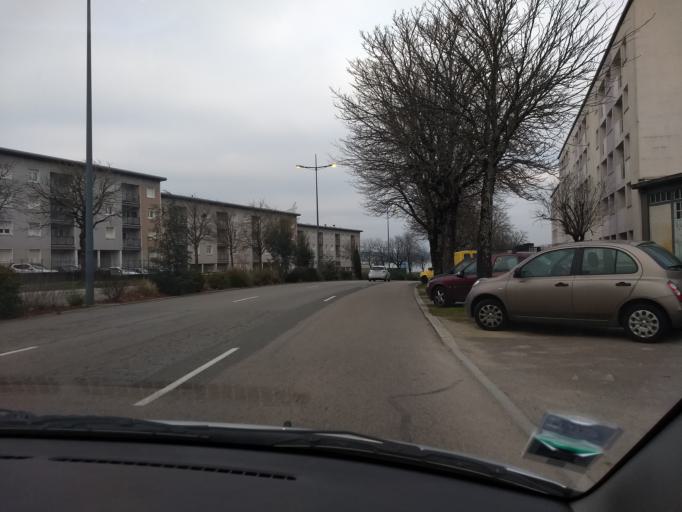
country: FR
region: Limousin
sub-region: Departement de la Haute-Vienne
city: Isle
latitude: 45.8251
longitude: 1.2258
